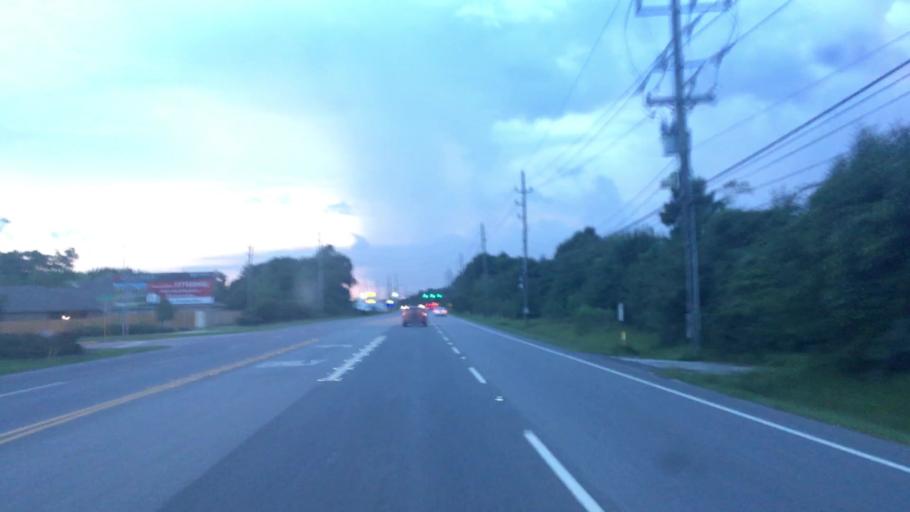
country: US
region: Texas
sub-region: Harris County
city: Humble
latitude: 29.9763
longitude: -95.2232
